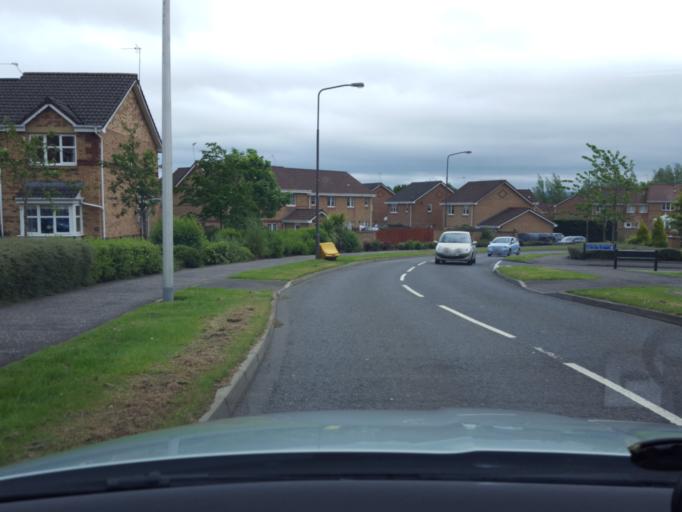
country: GB
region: Scotland
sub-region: West Lothian
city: Broxburn
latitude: 55.9289
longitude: -3.4958
